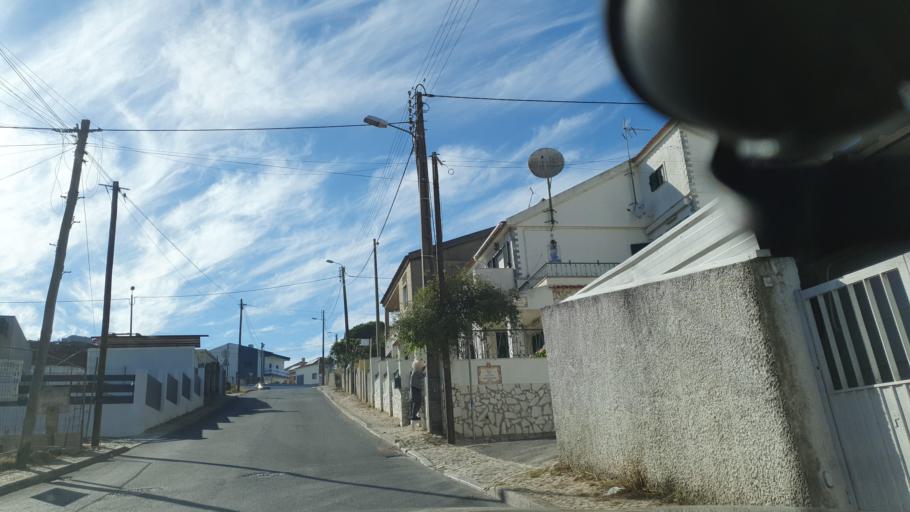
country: PT
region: Lisbon
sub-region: Sintra
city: Belas
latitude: 38.7960
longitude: -9.2521
